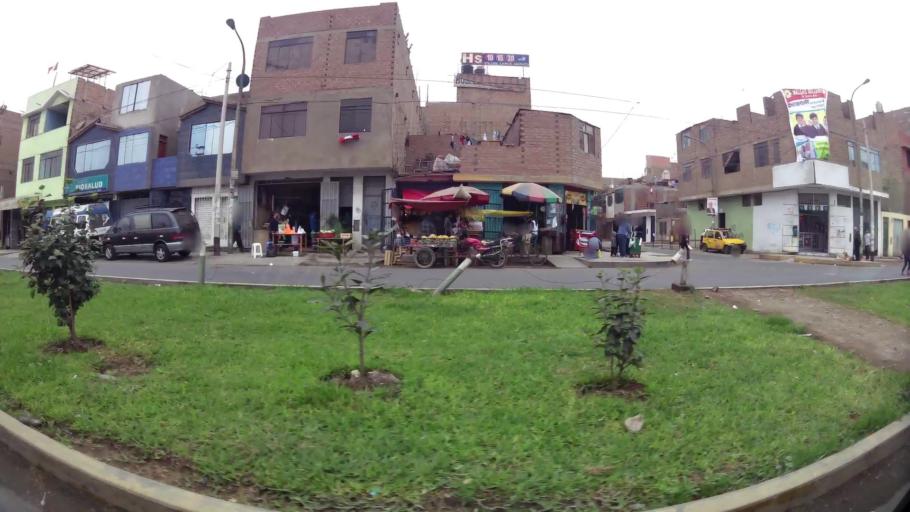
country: PE
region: Lima
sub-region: Lima
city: Independencia
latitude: -11.9518
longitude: -77.0802
